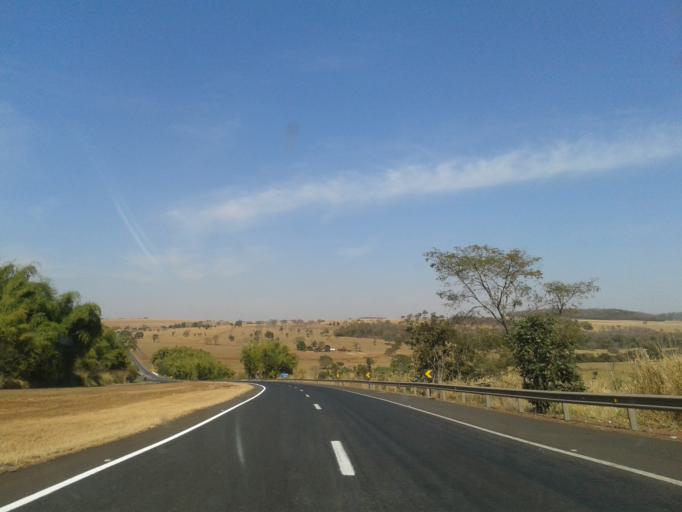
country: BR
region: Goias
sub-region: Goiatuba
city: Goiatuba
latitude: -18.1398
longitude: -49.2884
